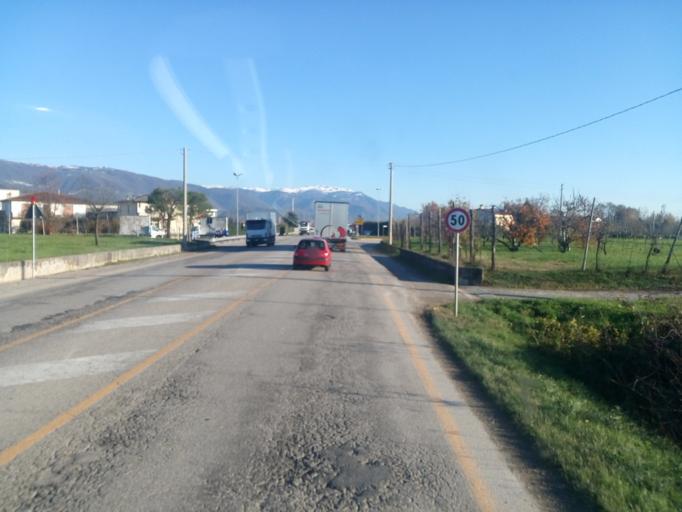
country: IT
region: Veneto
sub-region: Provincia di Vicenza
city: Schiavon
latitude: 45.7137
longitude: 11.6348
